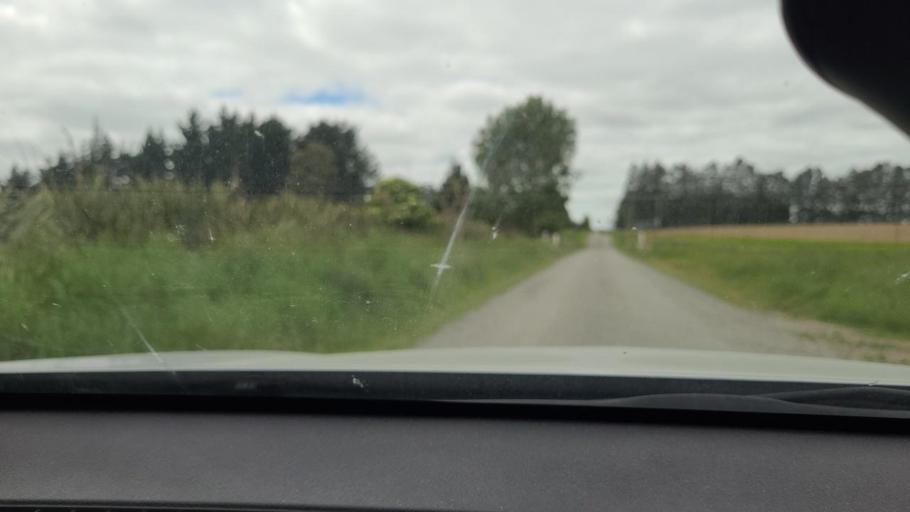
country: NZ
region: Southland
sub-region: Southland District
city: Riverton
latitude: -46.0831
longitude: 168.0075
